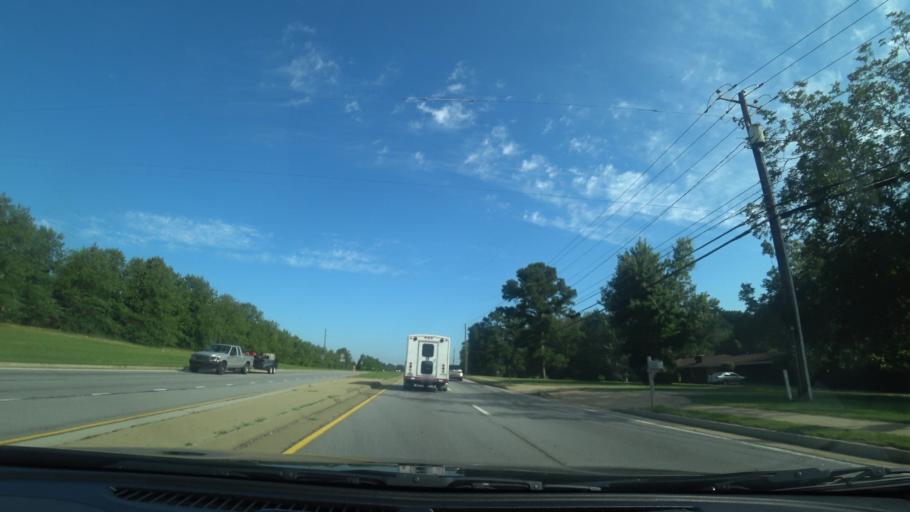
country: US
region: Georgia
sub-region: Gwinnett County
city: Grayson
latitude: 33.9158
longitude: -83.9712
